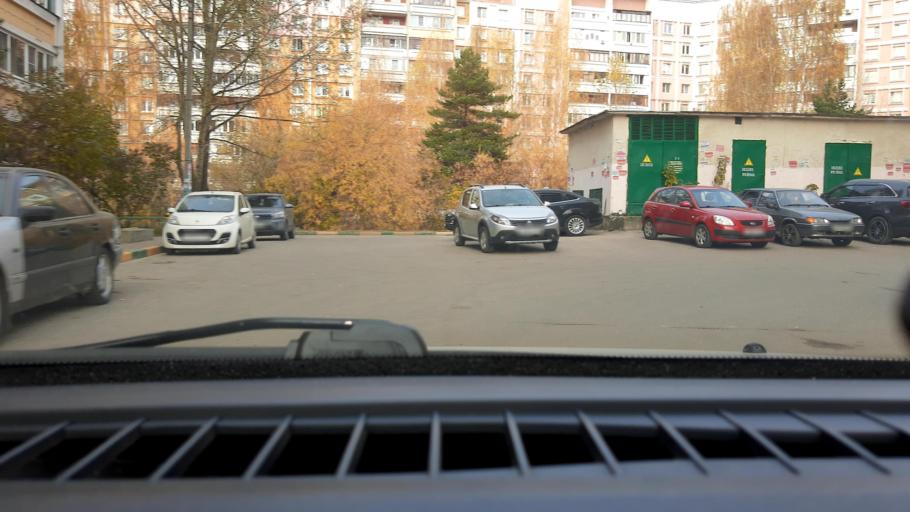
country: RU
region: Nizjnij Novgorod
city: Gorbatovka
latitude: 56.3662
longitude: 43.8012
